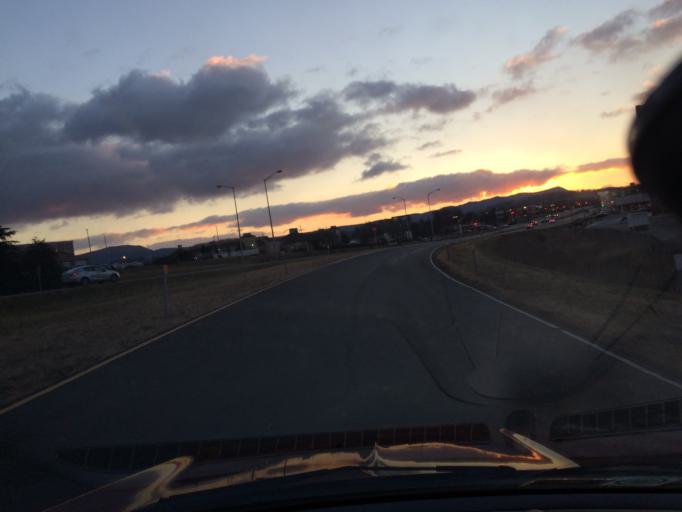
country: US
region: Virginia
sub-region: City of Harrisonburg
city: Harrisonburg
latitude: 38.4363
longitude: -78.8503
